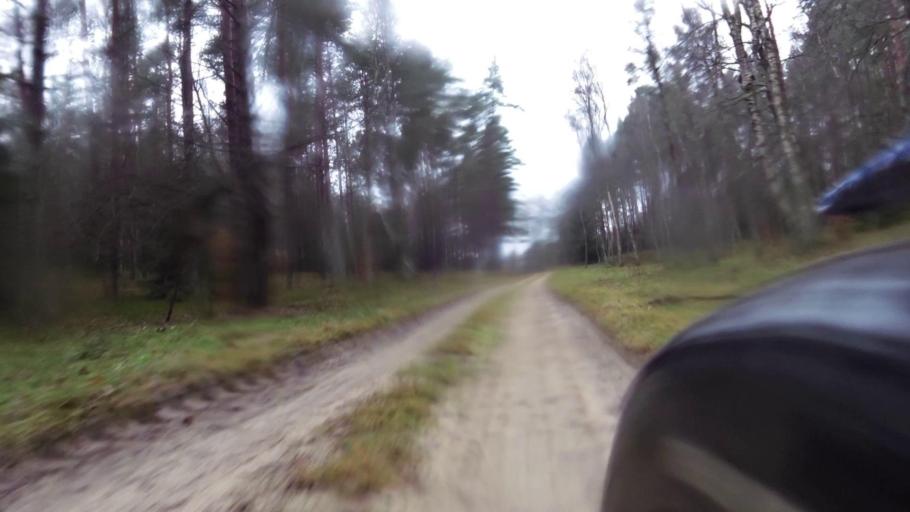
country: PL
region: West Pomeranian Voivodeship
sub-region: Powiat drawski
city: Zlocieniec
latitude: 53.5551
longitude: 15.9341
